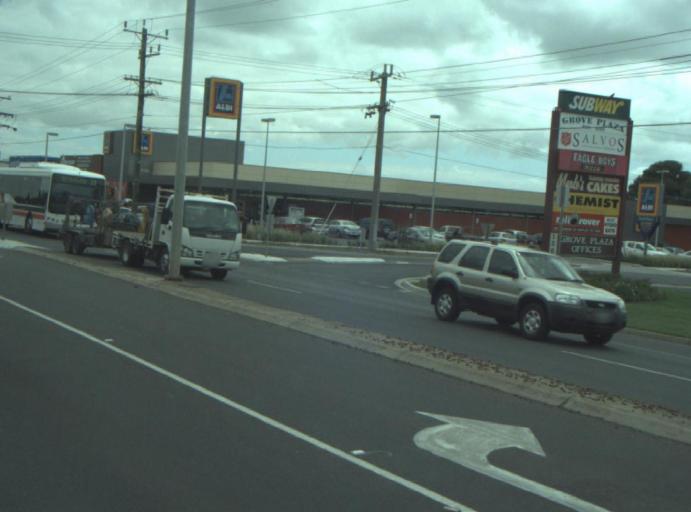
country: AU
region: Victoria
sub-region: Greater Geelong
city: Breakwater
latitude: -38.1941
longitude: 144.3426
